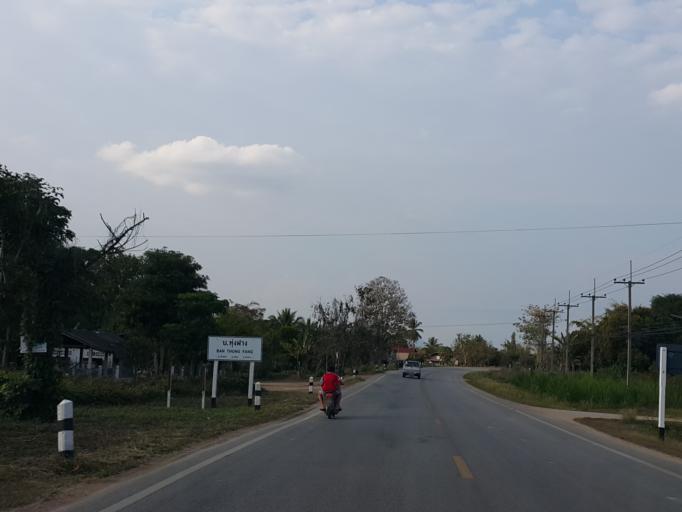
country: TH
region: Lampang
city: Lampang
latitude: 18.4982
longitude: 99.4719
